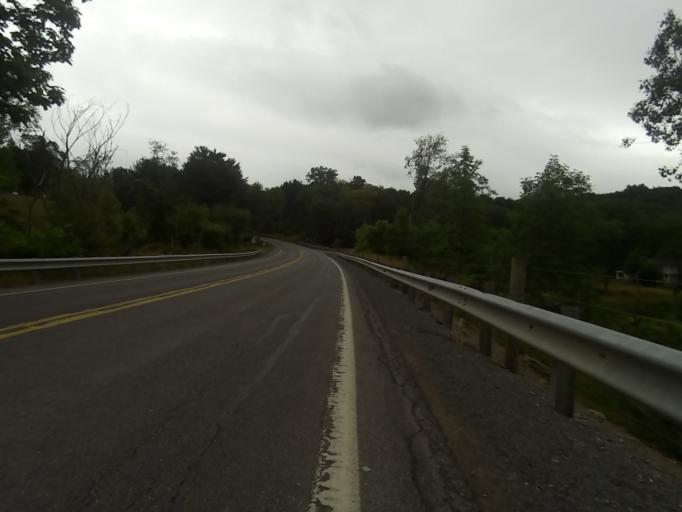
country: US
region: Pennsylvania
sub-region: Blair County
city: Tyrone
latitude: 40.6667
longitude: -78.1056
